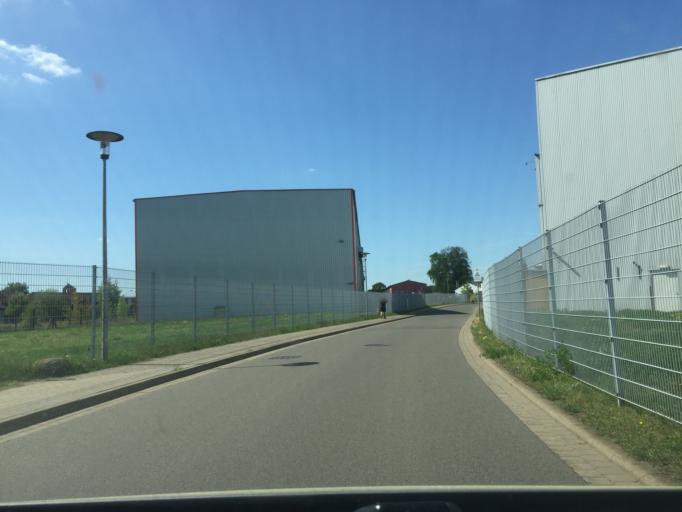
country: DE
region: Mecklenburg-Vorpommern
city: Torgelow
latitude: 53.6345
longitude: 14.0072
